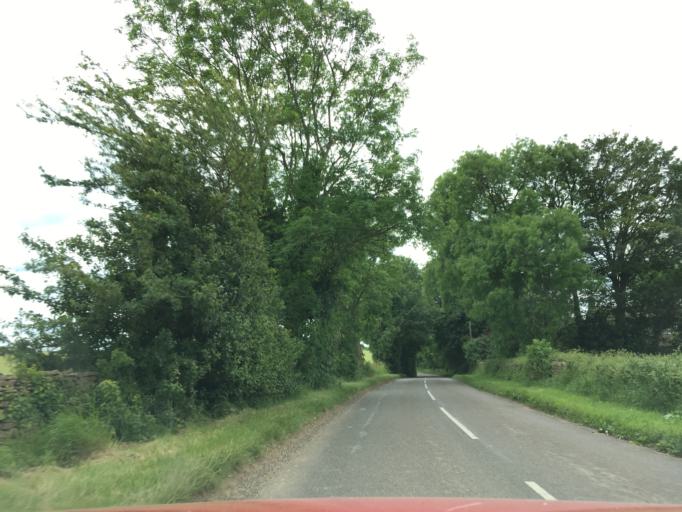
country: GB
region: England
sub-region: South Gloucestershire
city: Horton
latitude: 51.5206
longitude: -2.3338
